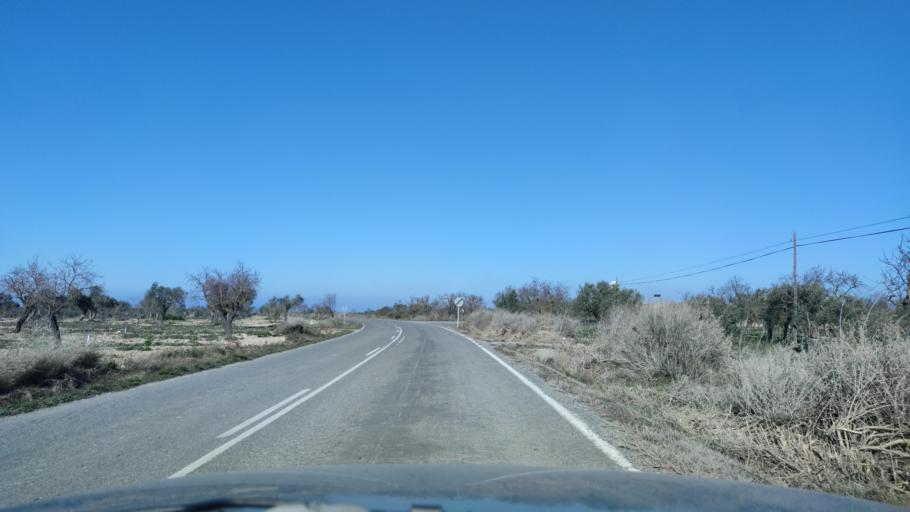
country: ES
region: Catalonia
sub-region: Provincia de Lleida
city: Maials
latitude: 41.3187
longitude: 0.4260
